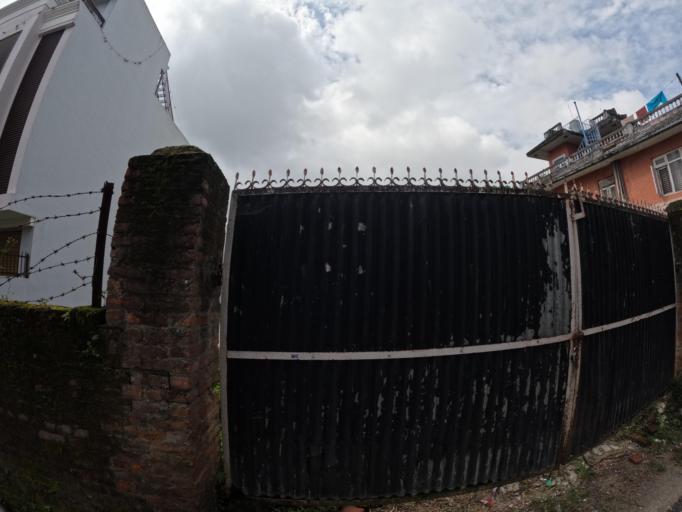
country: NP
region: Central Region
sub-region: Bagmati Zone
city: Kathmandu
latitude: 27.7512
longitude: 85.3240
